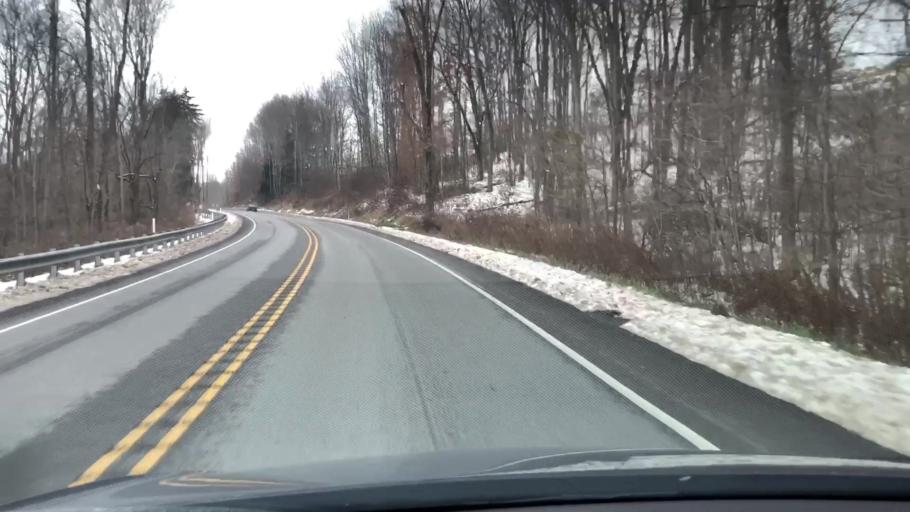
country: US
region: Pennsylvania
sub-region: Clearfield County
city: Treasure Lake
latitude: 41.1840
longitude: -78.6304
